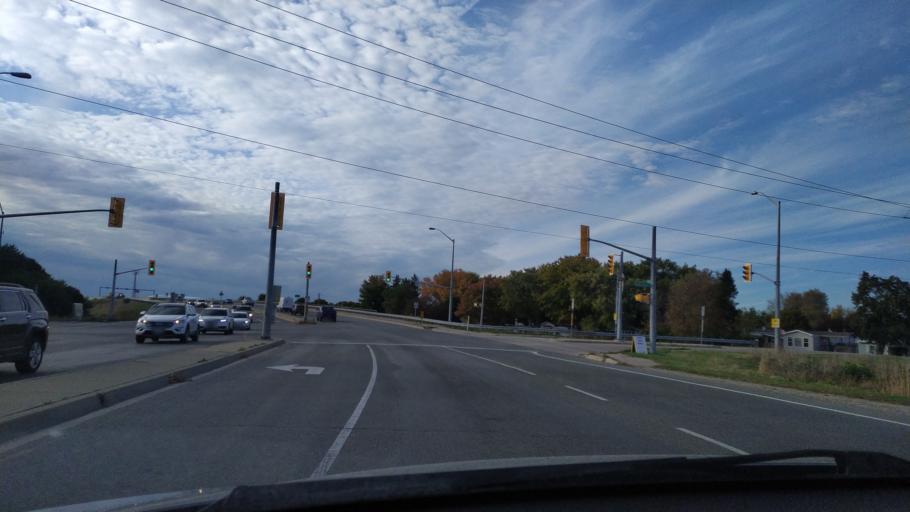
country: CA
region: Ontario
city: Waterloo
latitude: 43.5106
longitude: -80.5435
